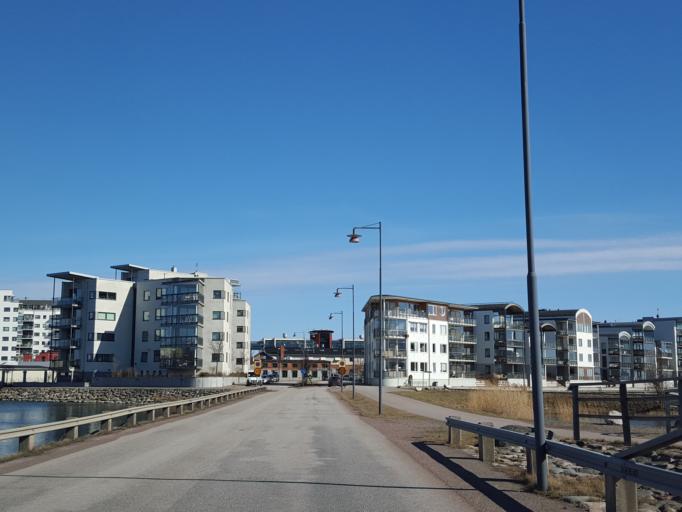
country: SE
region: Kalmar
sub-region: Kalmar Kommun
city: Kalmar
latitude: 56.6689
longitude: 16.3715
